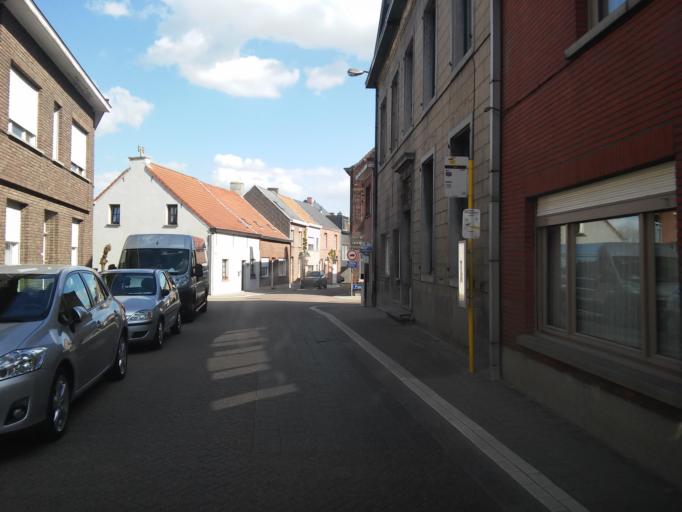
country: BE
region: Flanders
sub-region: Provincie Antwerpen
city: Puurs
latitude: 51.0916
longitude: 4.3058
